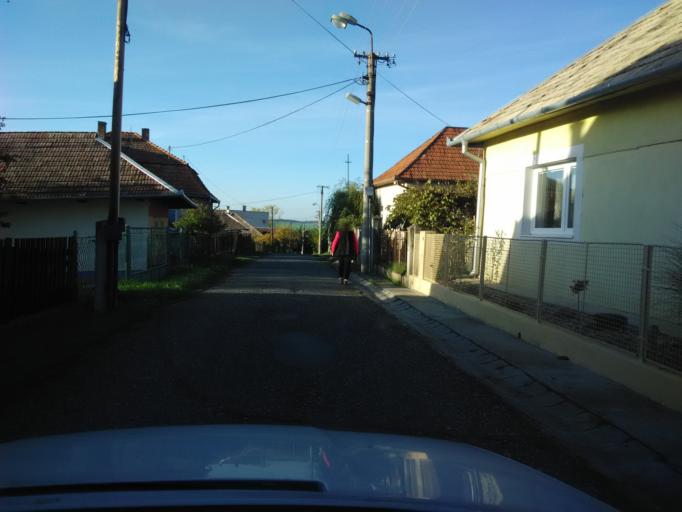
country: SK
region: Nitriansky
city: Svodin
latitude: 48.0382
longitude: 18.4693
